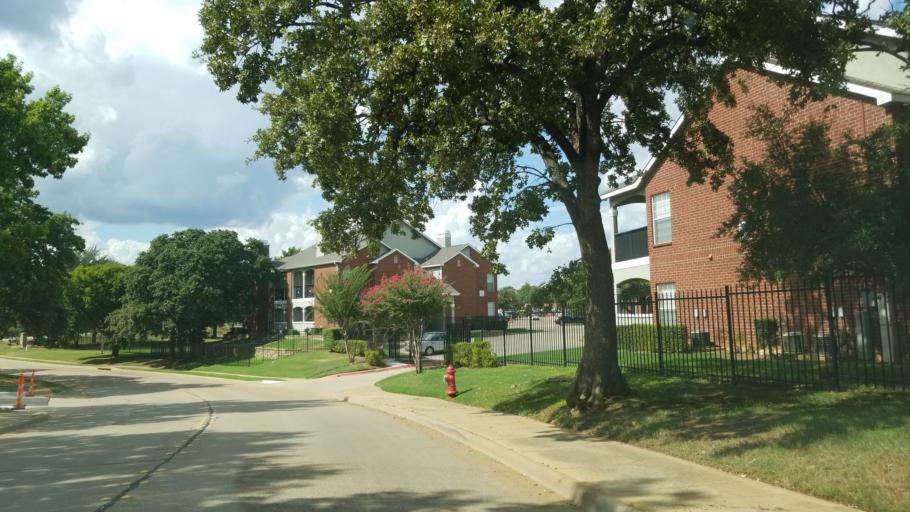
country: US
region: Texas
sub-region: Tarrant County
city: Euless
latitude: 32.8674
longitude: -97.0725
